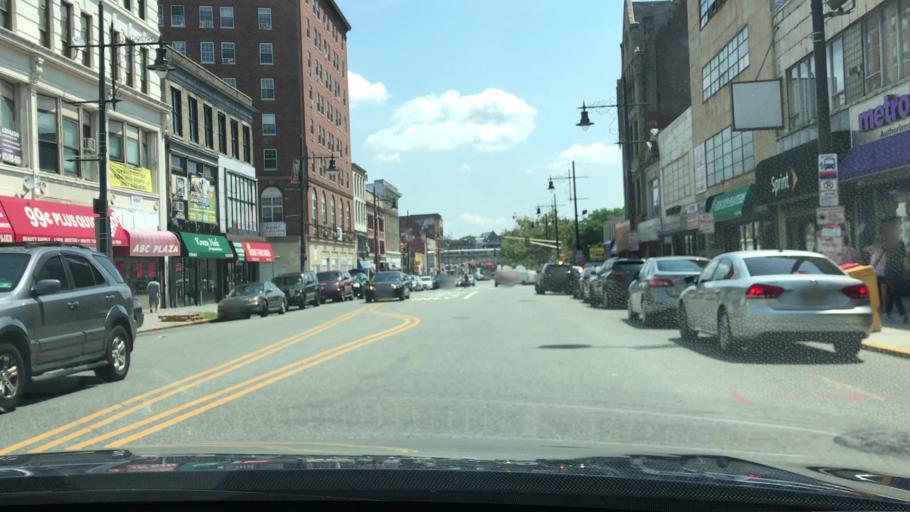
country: US
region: New Jersey
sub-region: Passaic County
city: Paterson
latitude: 40.9165
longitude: -74.1714
